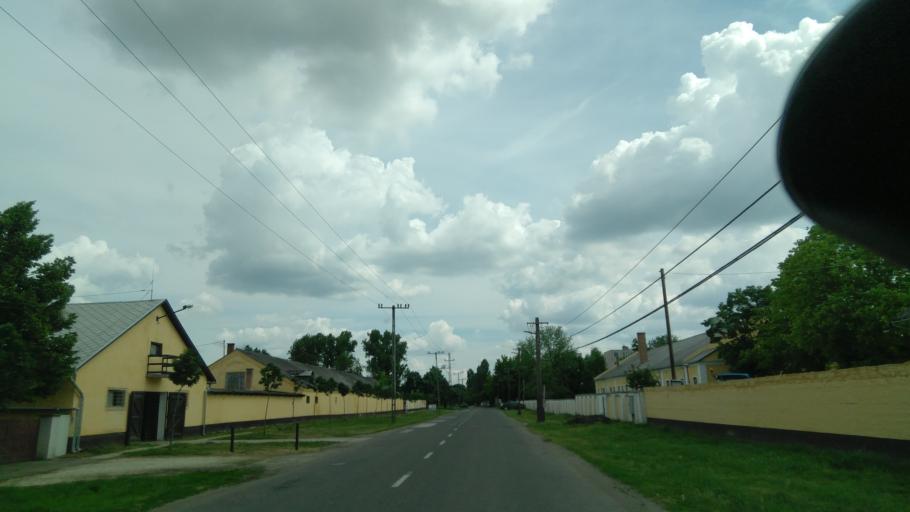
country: HU
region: Bekes
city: Mezohegyes
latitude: 46.3194
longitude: 20.8196
